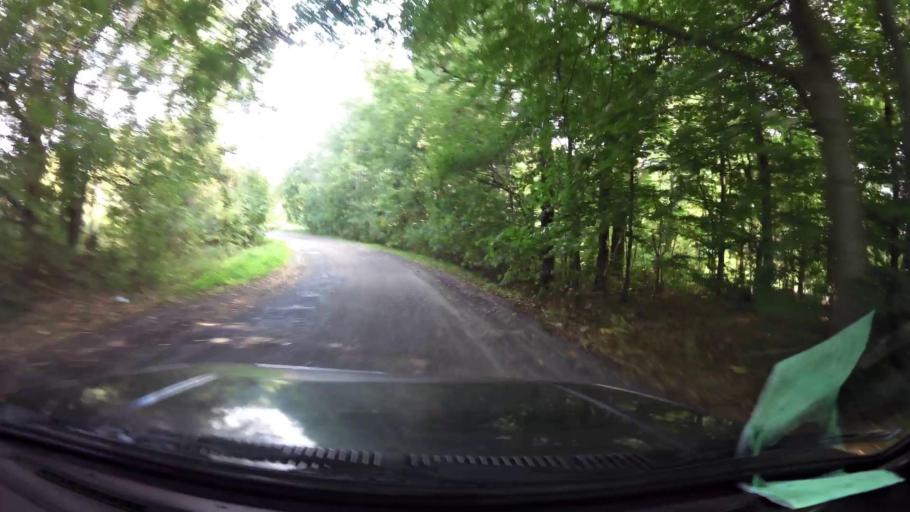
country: PL
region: West Pomeranian Voivodeship
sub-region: Powiat koszalinski
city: Polanow
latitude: 54.1291
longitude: 16.5199
